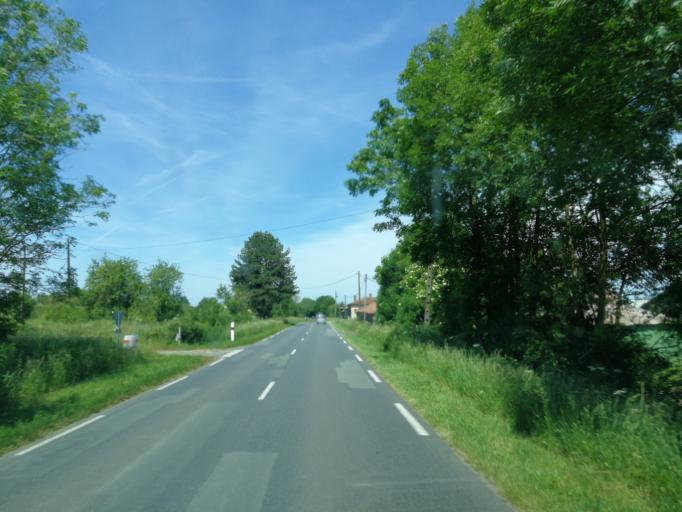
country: FR
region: Poitou-Charentes
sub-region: Departement des Deux-Sevres
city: La Foret-sur-Sevre
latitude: 46.7375
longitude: -0.6679
